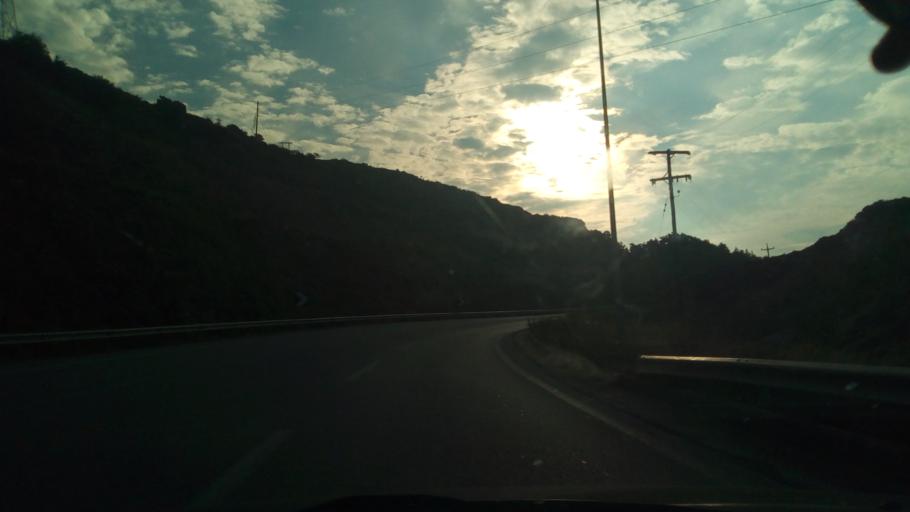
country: GR
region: West Greece
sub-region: Nomos Aitolias kai Akarnanias
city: Nafpaktos
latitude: 38.4011
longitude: 21.8136
